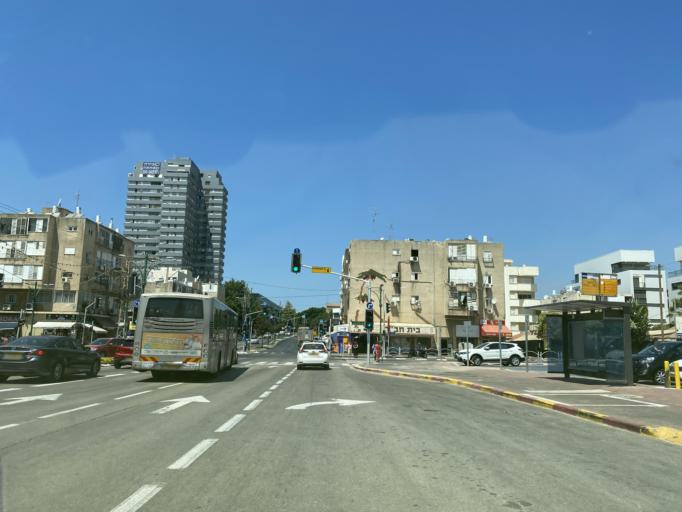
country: IL
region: Tel Aviv
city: Herzliyya
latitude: 32.1644
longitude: 34.8427
